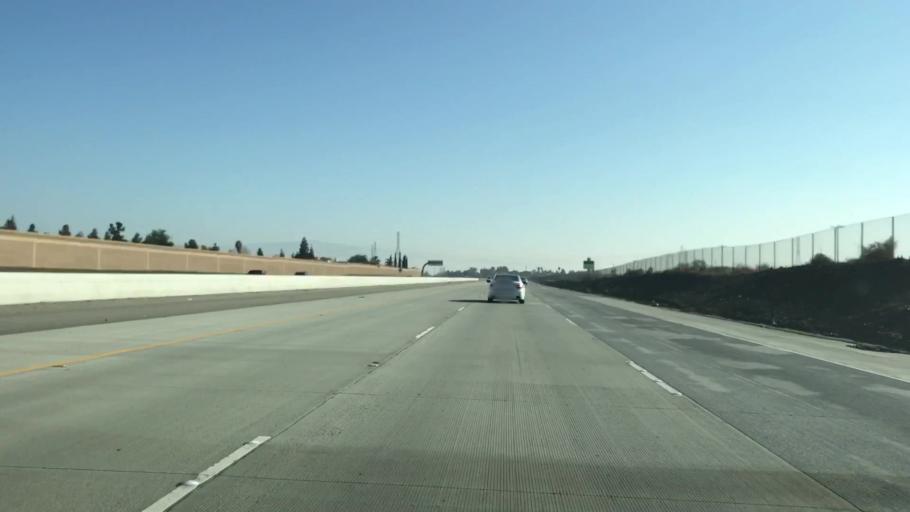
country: US
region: California
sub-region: Kern County
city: Greenacres
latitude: 35.3617
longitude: -119.1059
